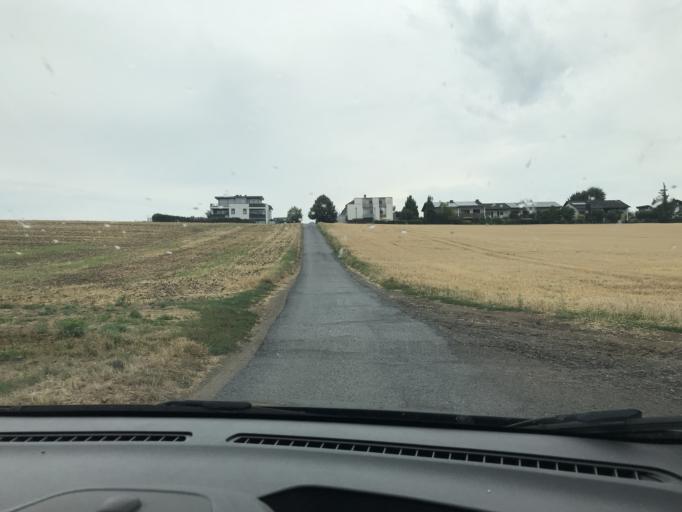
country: DE
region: Hesse
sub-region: Regierungsbezirk Darmstadt
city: Rossdorf
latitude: 49.8518
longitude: 8.7614
